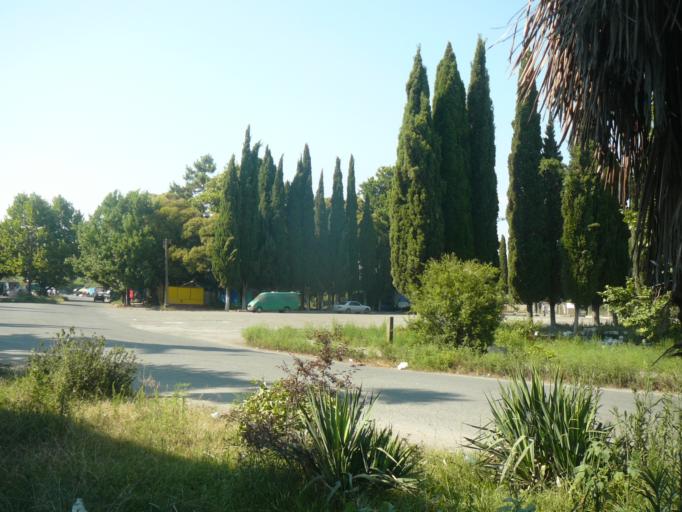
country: GE
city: Gantiadi
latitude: 43.3912
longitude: 40.0117
